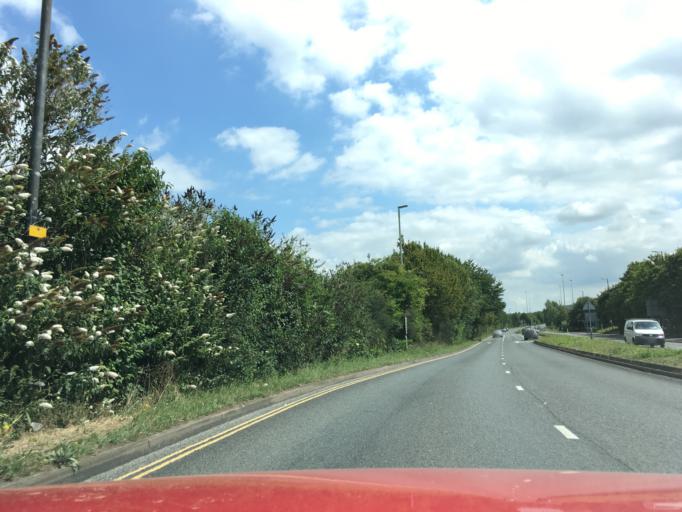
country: GB
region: England
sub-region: Gloucestershire
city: Gloucester
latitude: 51.8645
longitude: -2.2368
